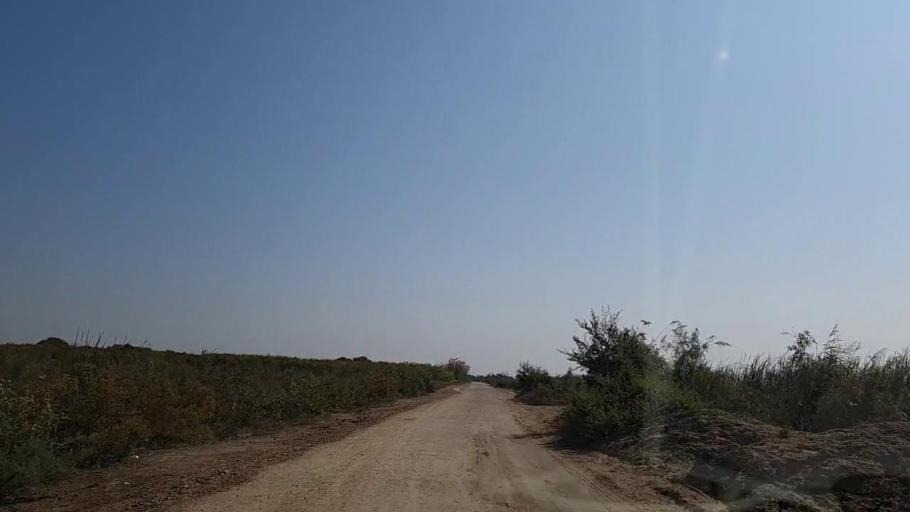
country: PK
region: Sindh
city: Chuhar Jamali
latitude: 24.4633
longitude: 68.1040
